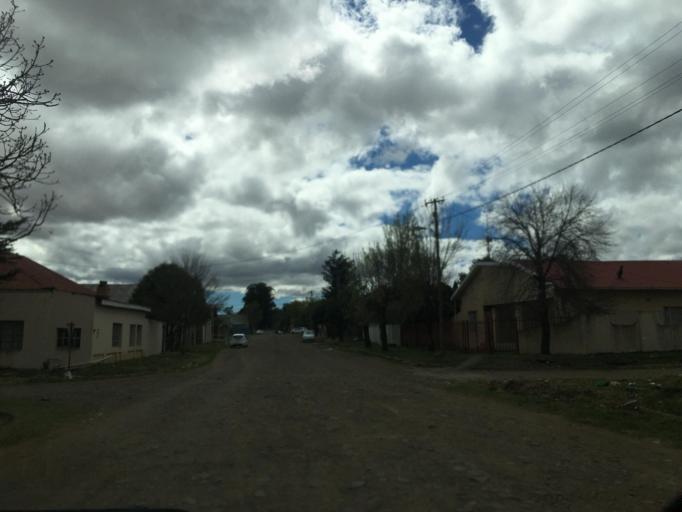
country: ZA
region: Eastern Cape
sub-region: Chris Hani District Municipality
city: Elliot
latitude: -31.3363
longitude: 27.8503
